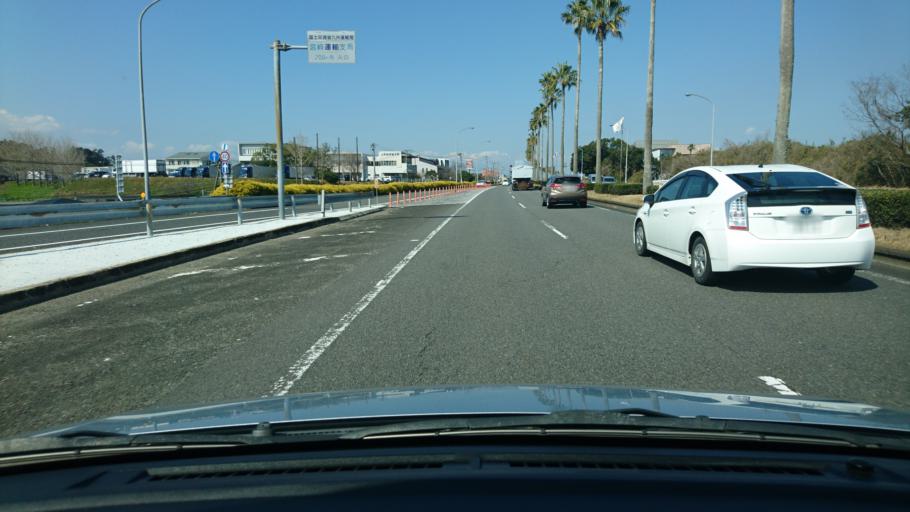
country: JP
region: Miyazaki
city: Miyazaki-shi
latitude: 31.8726
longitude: 131.4138
